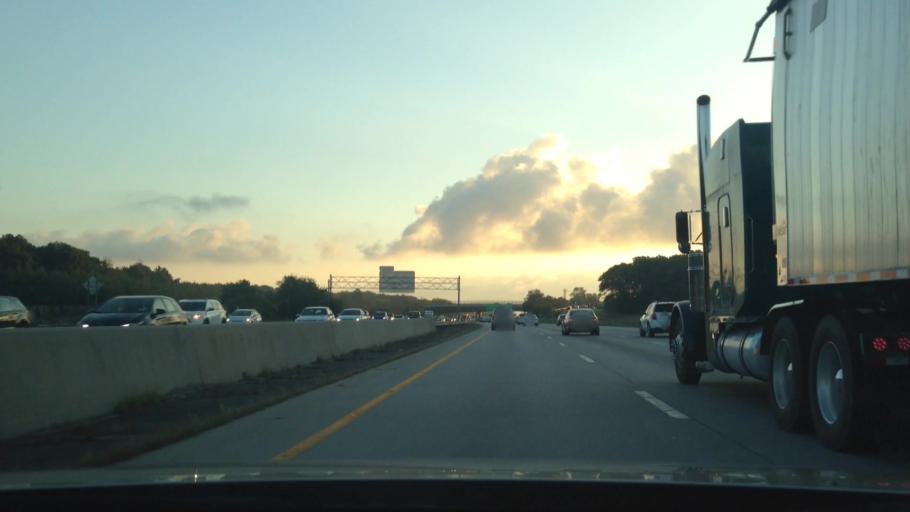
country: US
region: New York
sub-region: Suffolk County
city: Oakdale
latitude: 40.7503
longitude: -73.1307
